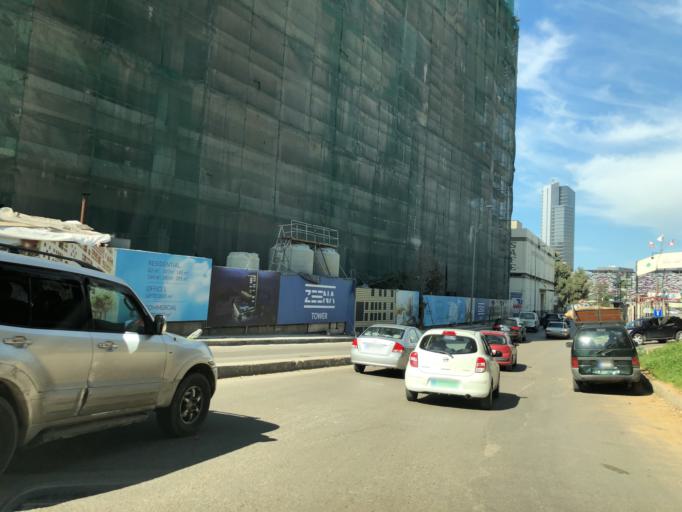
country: LB
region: Mont-Liban
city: Jdaidet el Matn
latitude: 33.8807
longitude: 35.5312
